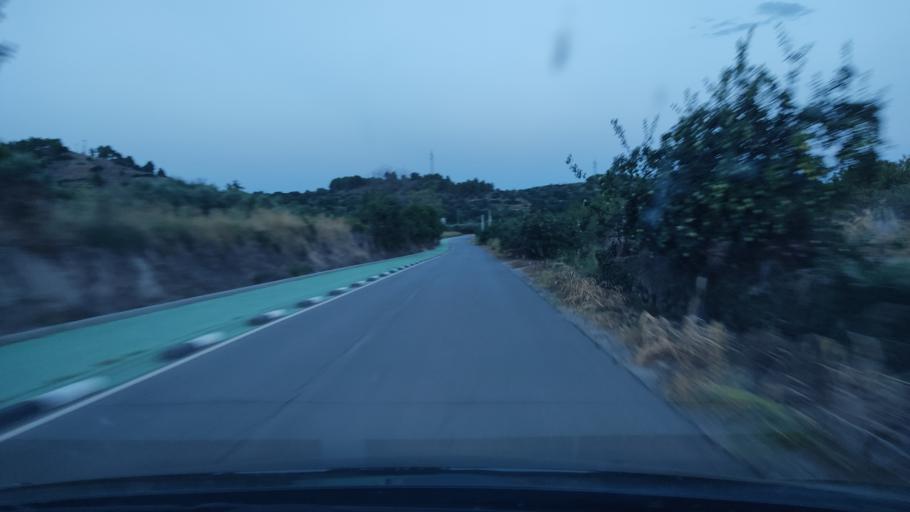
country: ES
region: Valencia
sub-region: Provincia de Castello
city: Jerica
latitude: 39.9094
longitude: -0.5644
